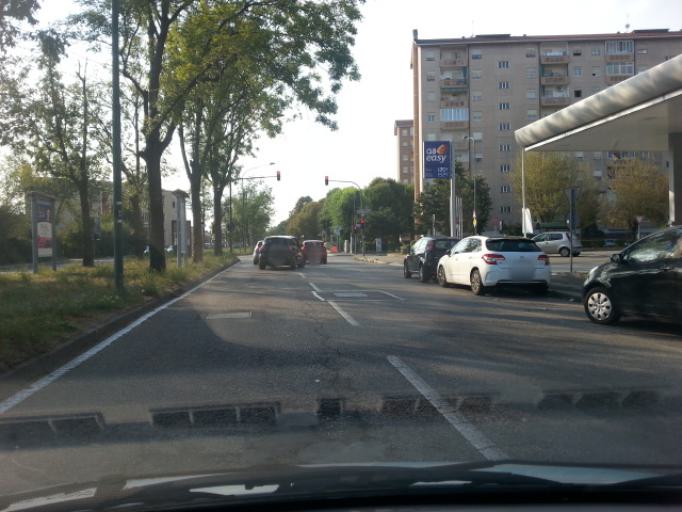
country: IT
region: Piedmont
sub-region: Provincia di Torino
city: Fornaci
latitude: 45.0167
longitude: 7.6105
